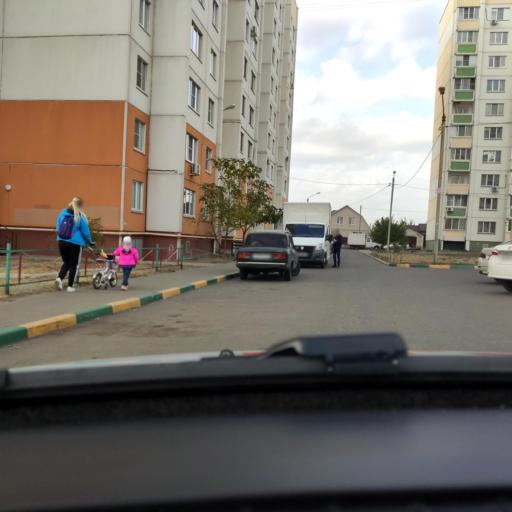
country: RU
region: Voronezj
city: Shilovo
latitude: 51.5616
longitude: 39.1120
